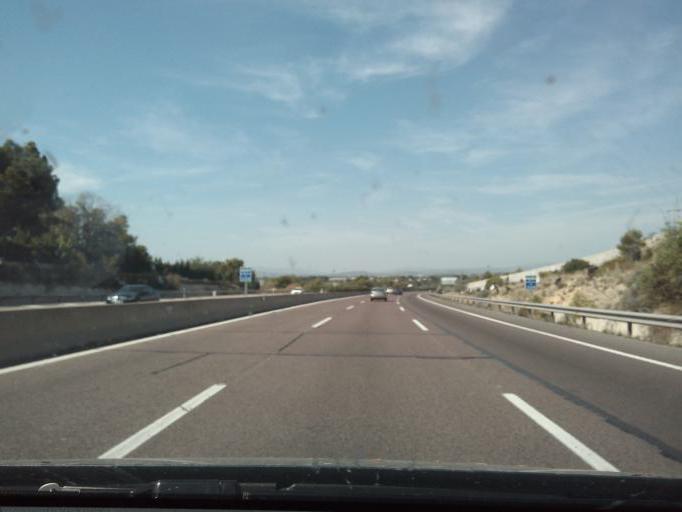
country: ES
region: Valencia
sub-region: Provincia de Valencia
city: Manises
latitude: 39.5161
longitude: -0.4820
